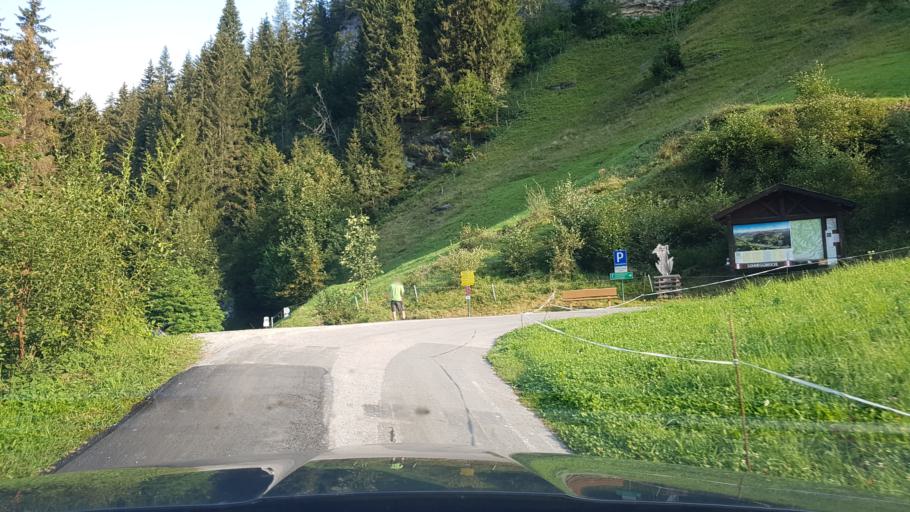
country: AT
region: Salzburg
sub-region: Politischer Bezirk Sankt Johann im Pongau
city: Kleinarl
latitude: 47.2757
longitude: 13.2414
